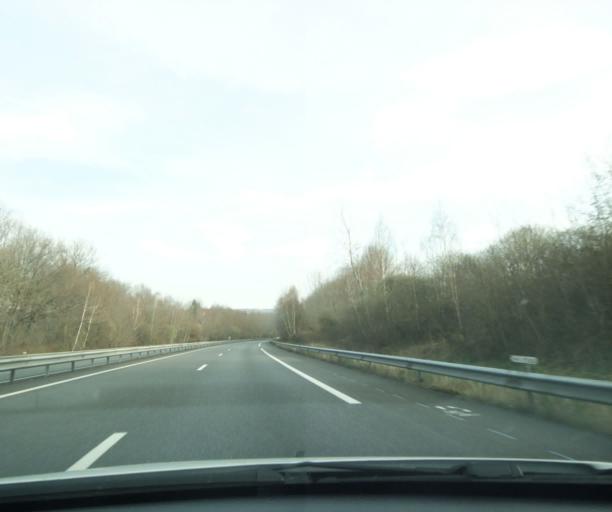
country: FR
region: Midi-Pyrenees
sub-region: Departement des Hautes-Pyrenees
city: Tournay
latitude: 43.1984
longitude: 0.2118
